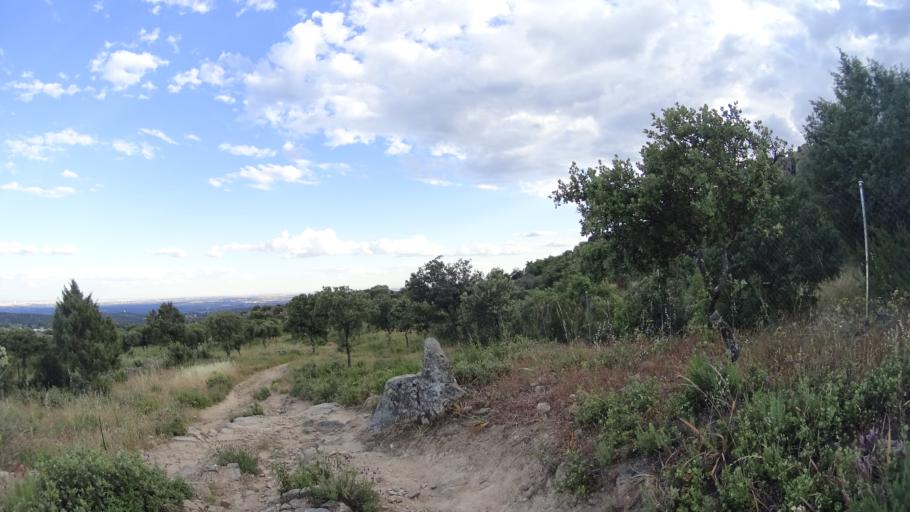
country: ES
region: Madrid
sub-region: Provincia de Madrid
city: Hoyo de Manzanares
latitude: 40.6312
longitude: -3.9122
